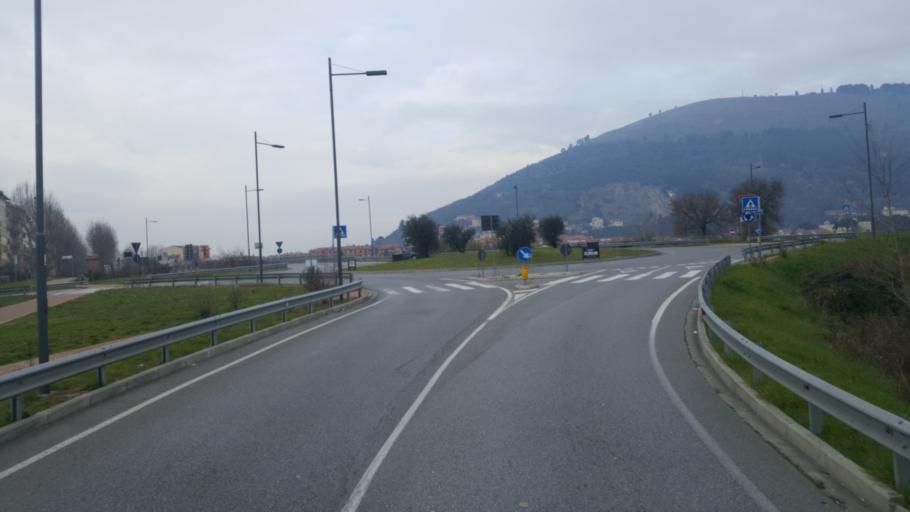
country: IT
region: Tuscany
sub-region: Province of Florence
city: Calenzano
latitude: 43.8580
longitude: 11.1455
